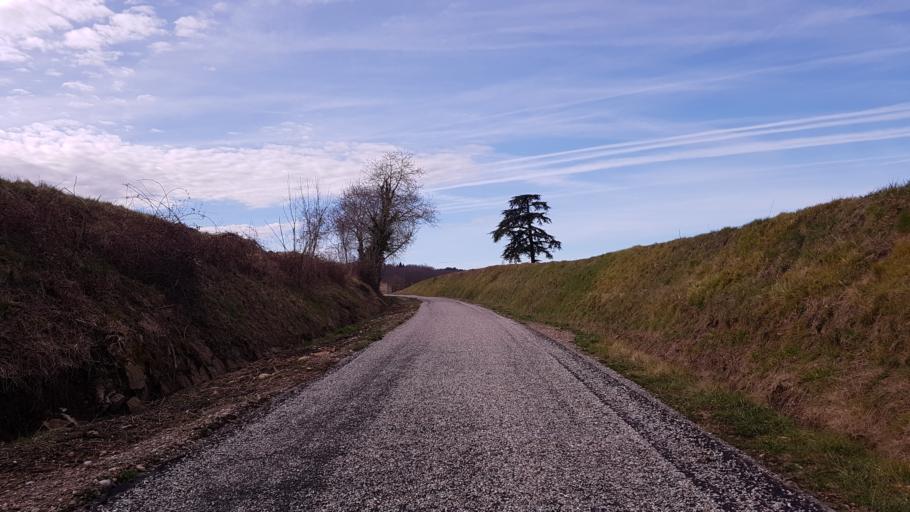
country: FR
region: Languedoc-Roussillon
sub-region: Departement de l'Aude
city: Chalabre
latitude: 42.9558
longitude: 1.9829
